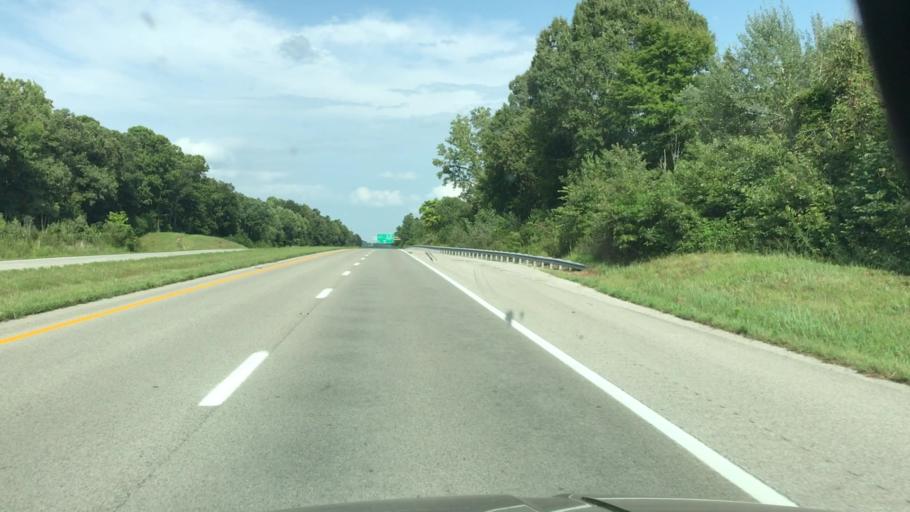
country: US
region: Kentucky
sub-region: Hopkins County
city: Nortonville
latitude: 37.2078
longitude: -87.4956
